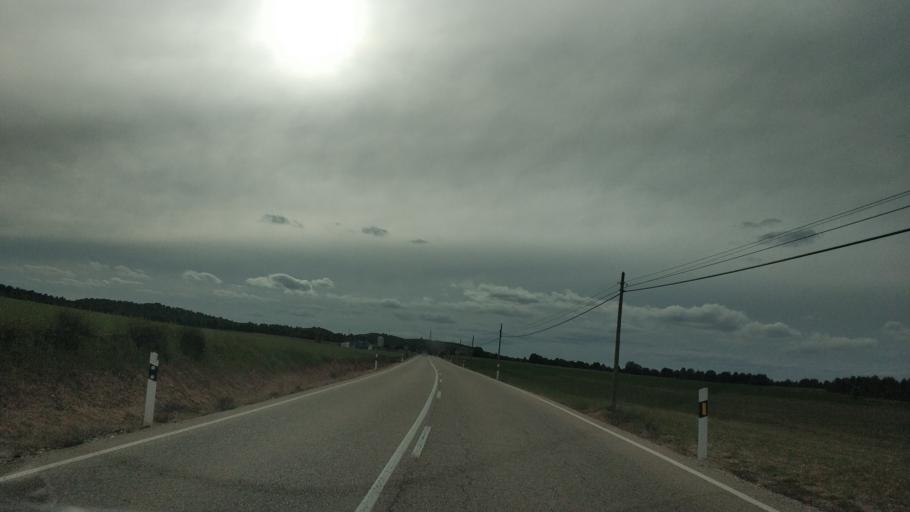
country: ES
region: Castille and Leon
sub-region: Provincia de Soria
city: El Burgo de Osma
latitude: 41.5745
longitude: -3.0198
